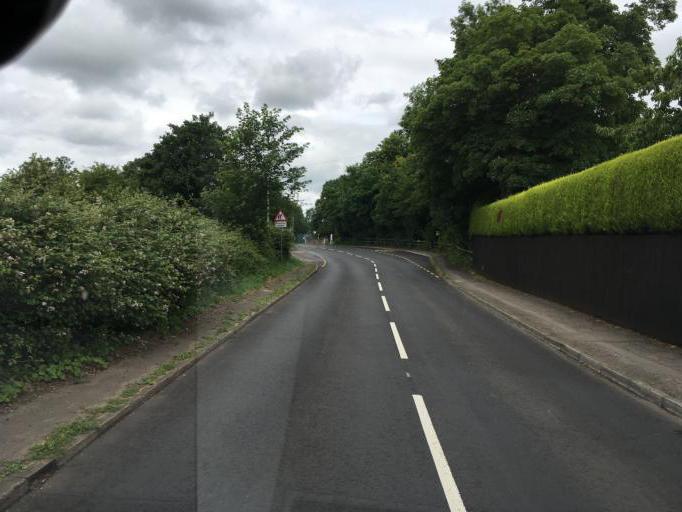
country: GB
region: England
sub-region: Gloucestershire
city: Stonehouse
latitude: 51.7521
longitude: -2.3157
